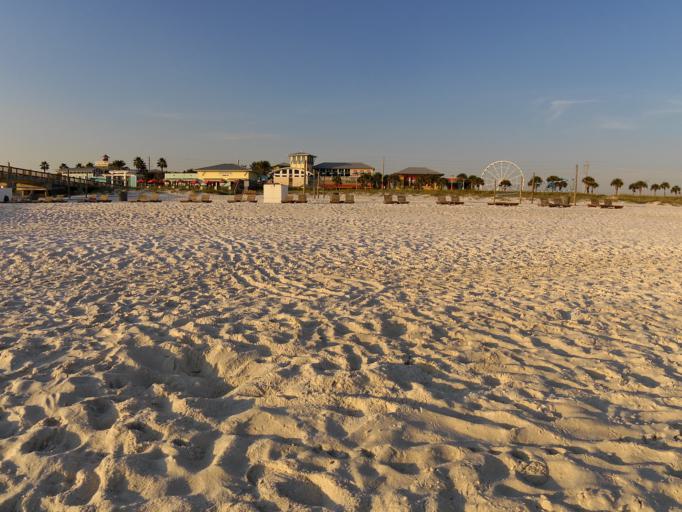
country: US
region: Florida
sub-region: Bay County
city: Laguna Beach
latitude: 30.2145
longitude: -85.8773
